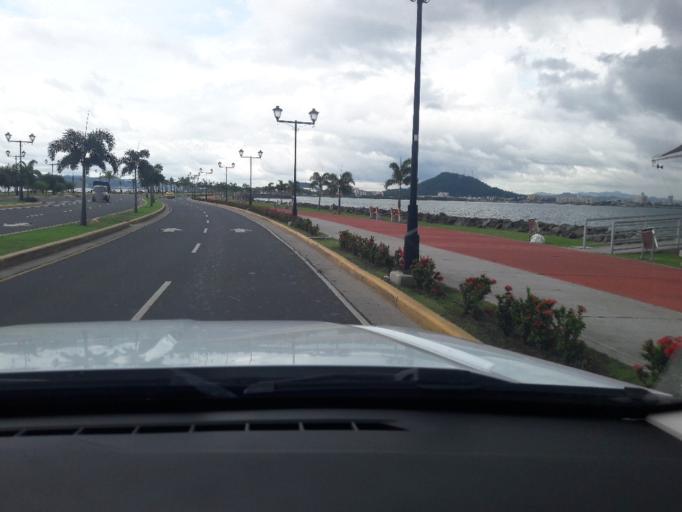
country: PA
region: Panama
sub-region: Distrito de Panama
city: Ancon
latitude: 8.9201
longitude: -79.5356
